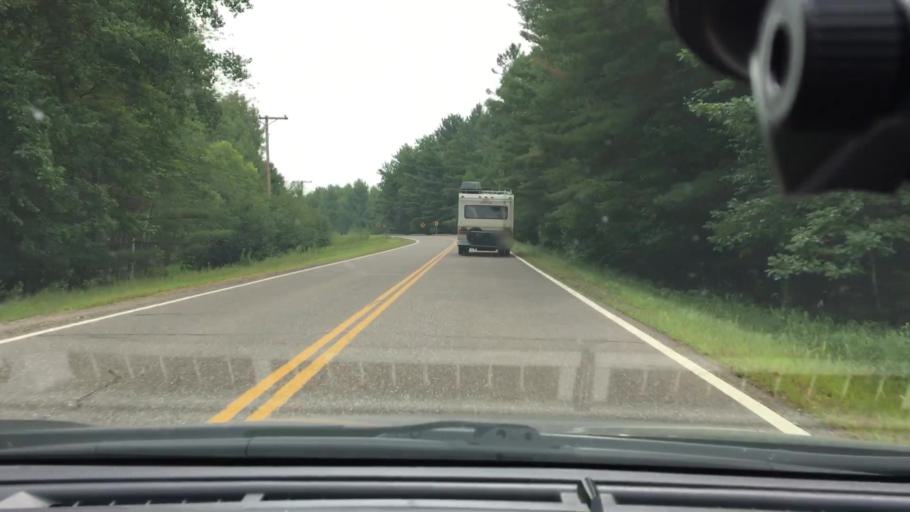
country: US
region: Minnesota
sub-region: Aitkin County
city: Aitkin
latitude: 46.4020
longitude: -93.7743
